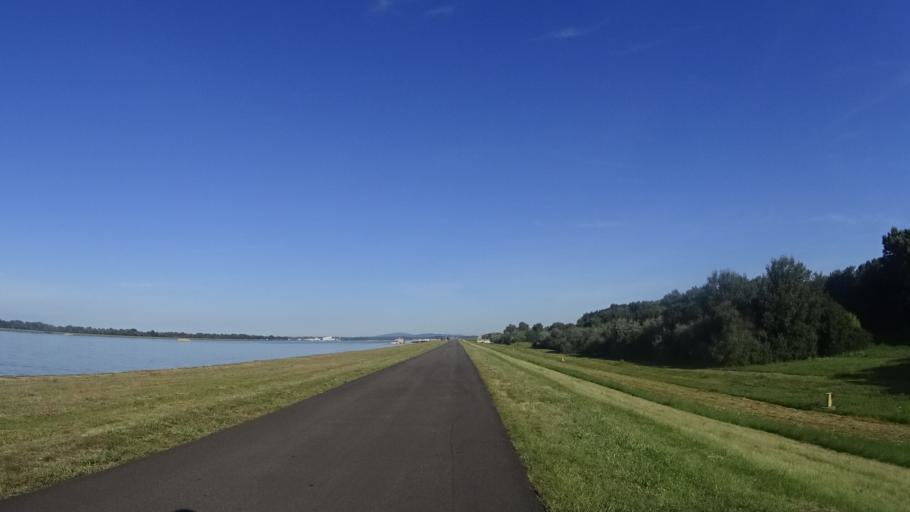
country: SK
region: Trnavsky
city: Samorin
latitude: 48.0296
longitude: 17.2567
